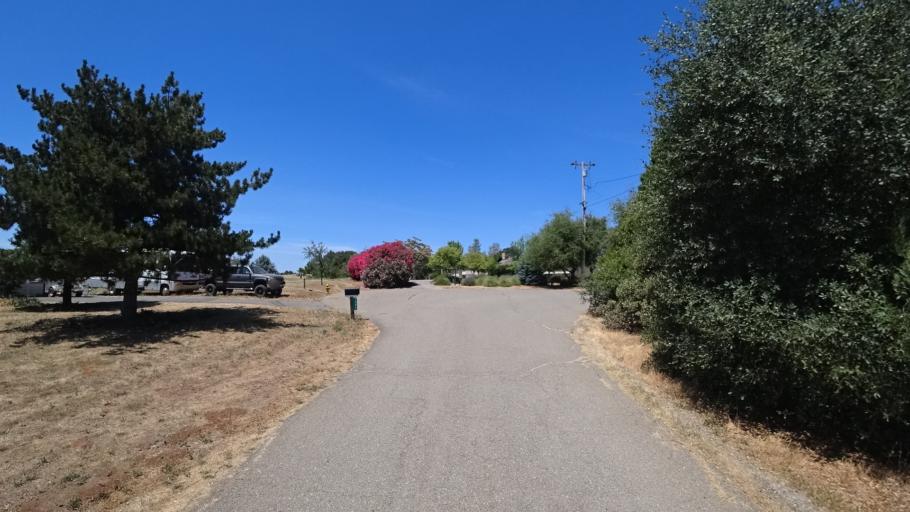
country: US
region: California
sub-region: Amador County
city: Jackson
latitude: 38.2943
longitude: -120.7089
